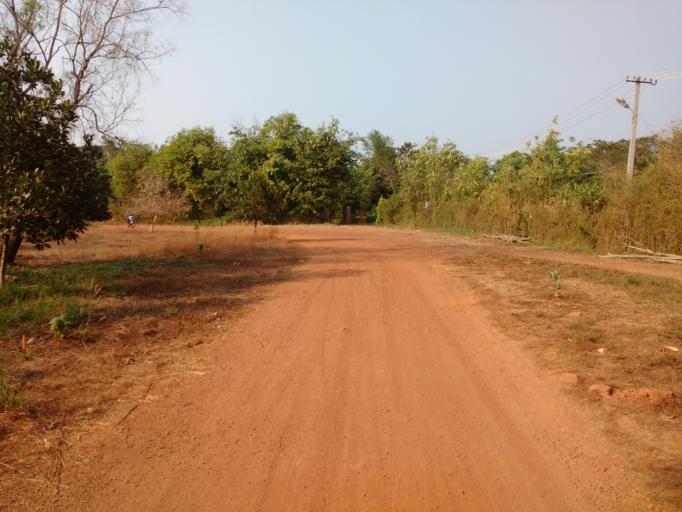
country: IN
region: Karnataka
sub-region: Dakshina Kannada
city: Mangalore
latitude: 12.9300
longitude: 74.9035
